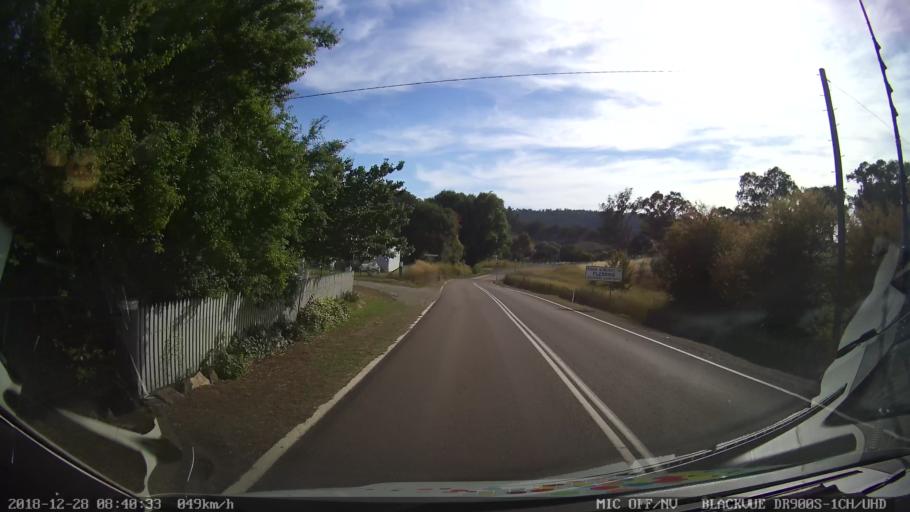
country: AU
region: New South Wales
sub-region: Upper Lachlan Shire
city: Crookwell
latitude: -34.0135
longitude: 149.3224
